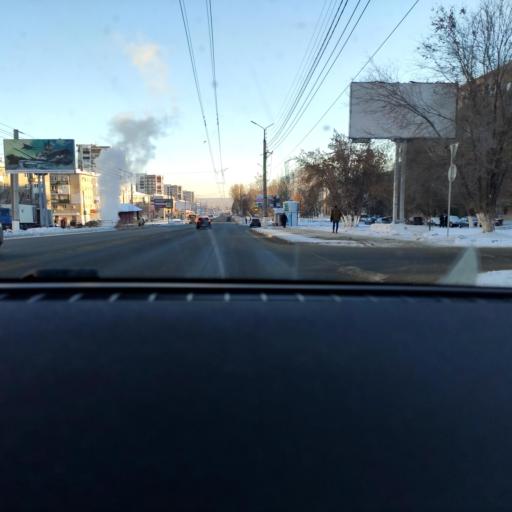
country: RU
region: Samara
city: Novokuybyshevsk
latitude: 53.0929
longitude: 49.9800
